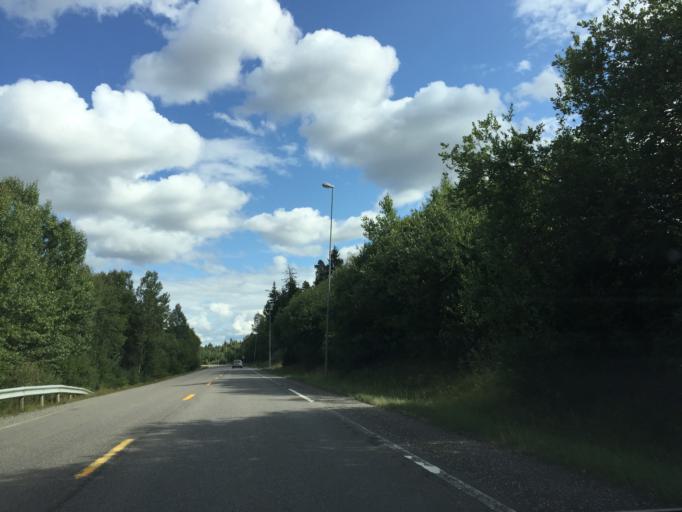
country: NO
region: Ostfold
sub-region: Hobol
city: Knappstad
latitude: 59.6180
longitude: 11.0336
